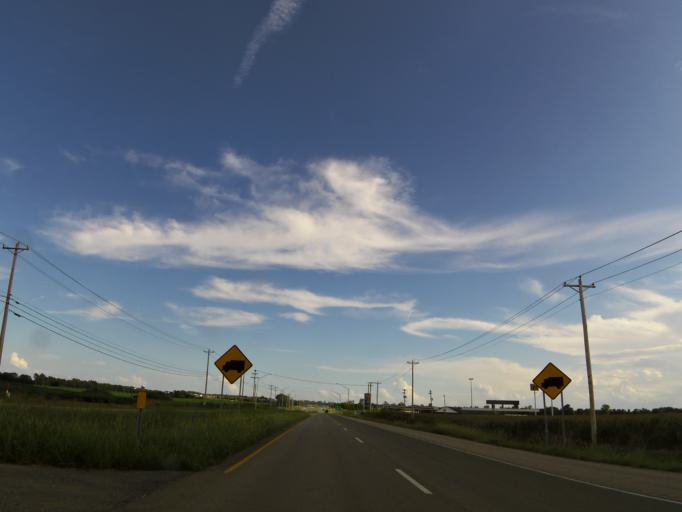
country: US
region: Kentucky
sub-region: Christian County
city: Oak Grove
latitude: 36.7119
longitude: -87.4578
